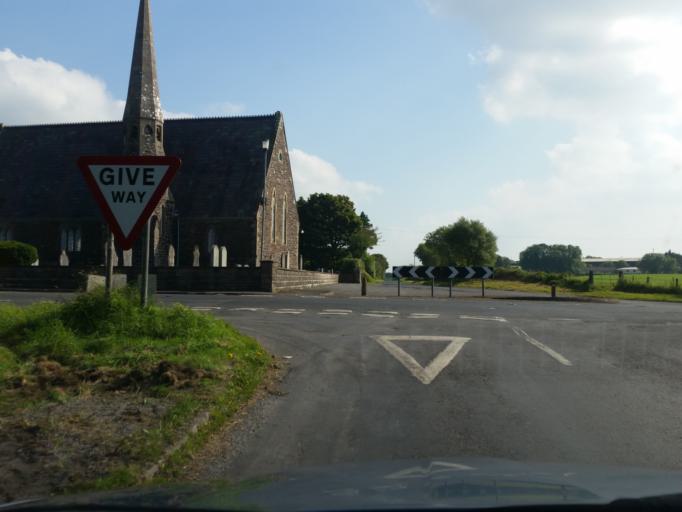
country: GB
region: Northern Ireland
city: Ballinamallard
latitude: 54.3634
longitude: -7.5639
